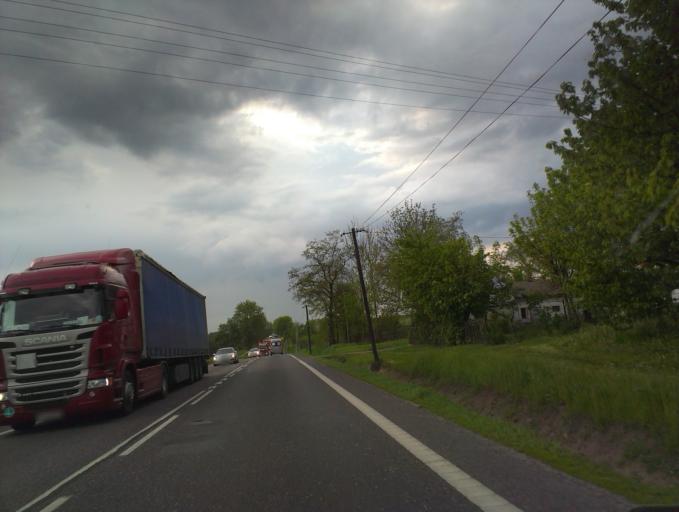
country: PL
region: Masovian Voivodeship
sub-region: Powiat grojecki
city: Pniewy
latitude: 51.9190
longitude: 20.6778
